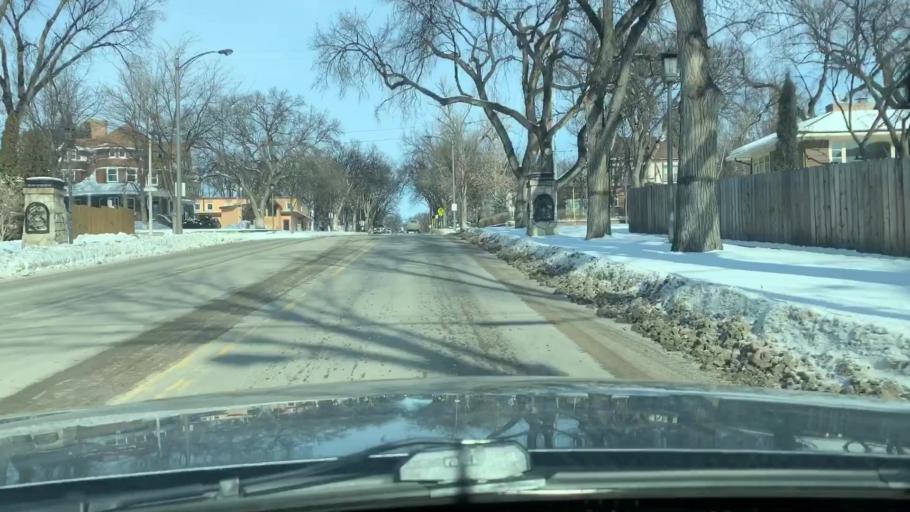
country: US
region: North Dakota
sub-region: Burleigh County
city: Bismarck
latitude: 46.8092
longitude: -100.7943
